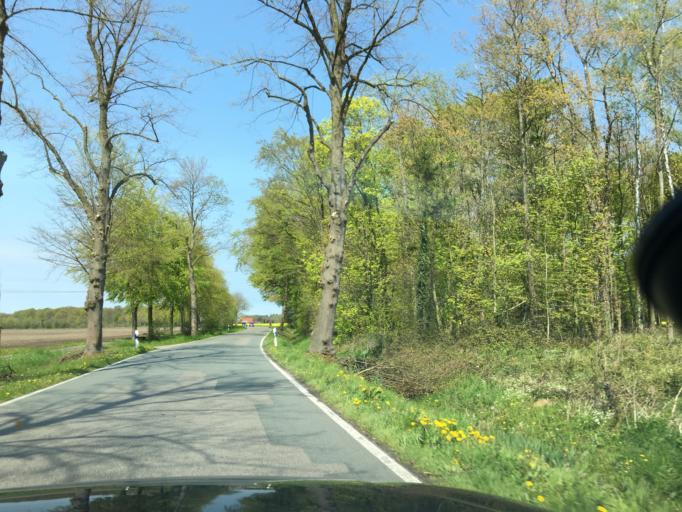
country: DE
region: North Rhine-Westphalia
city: Ludinghausen
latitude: 51.7807
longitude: 7.4371
